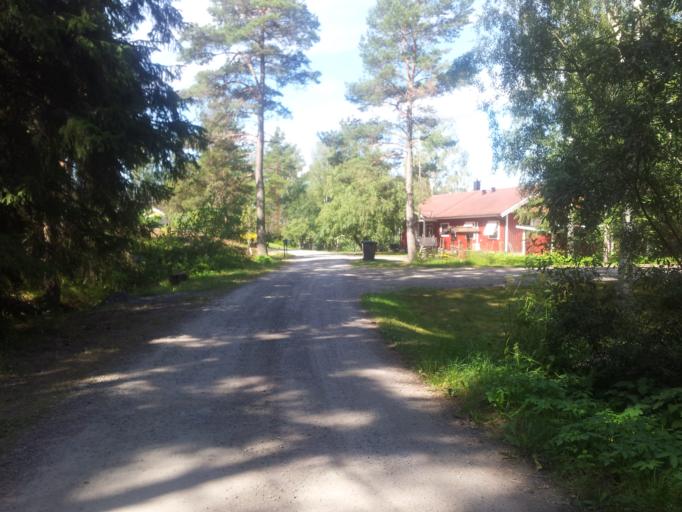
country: SE
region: Stockholm
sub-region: Norrtalje Kommun
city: Nykvarn
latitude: 59.9001
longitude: 18.2554
